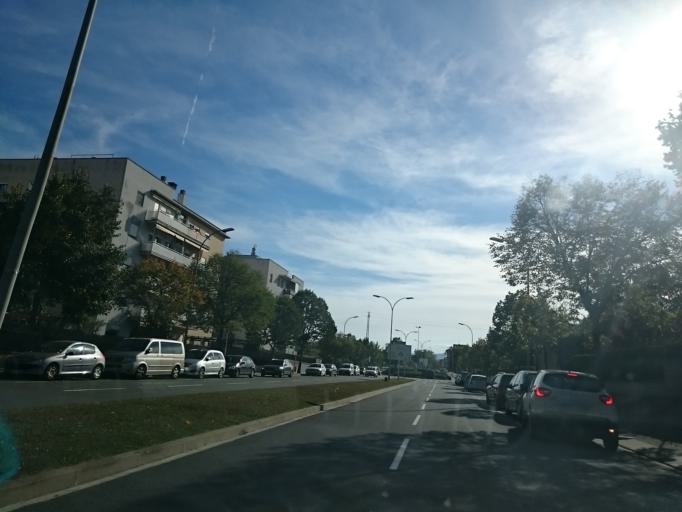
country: ES
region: Catalonia
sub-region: Provincia de Barcelona
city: Vic
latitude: 41.9271
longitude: 2.2647
